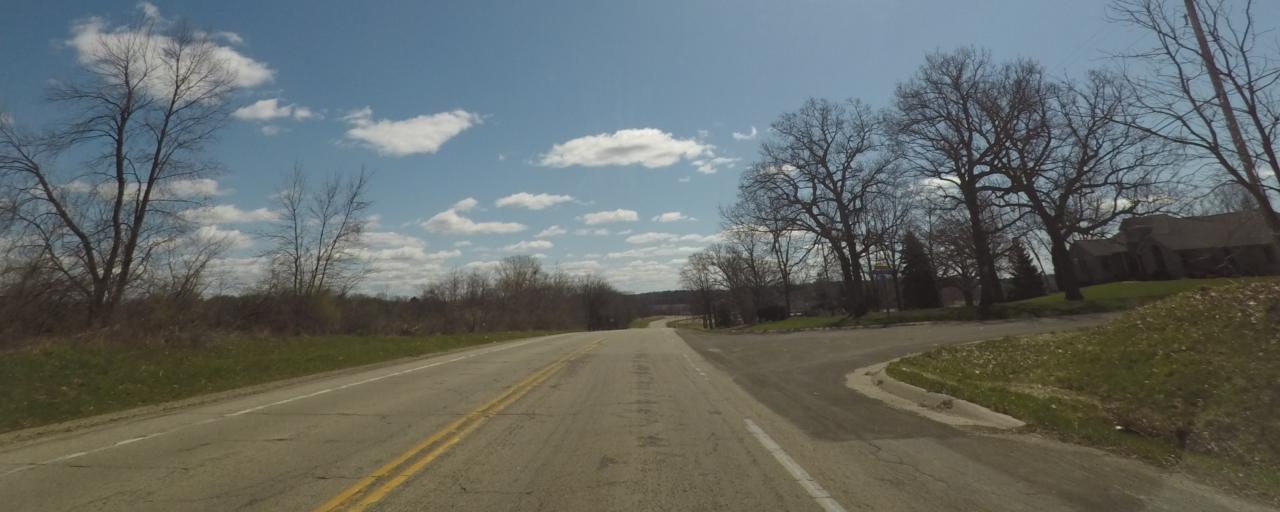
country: US
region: Wisconsin
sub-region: Dane County
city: Cottage Grove
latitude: 43.0916
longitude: -89.1788
